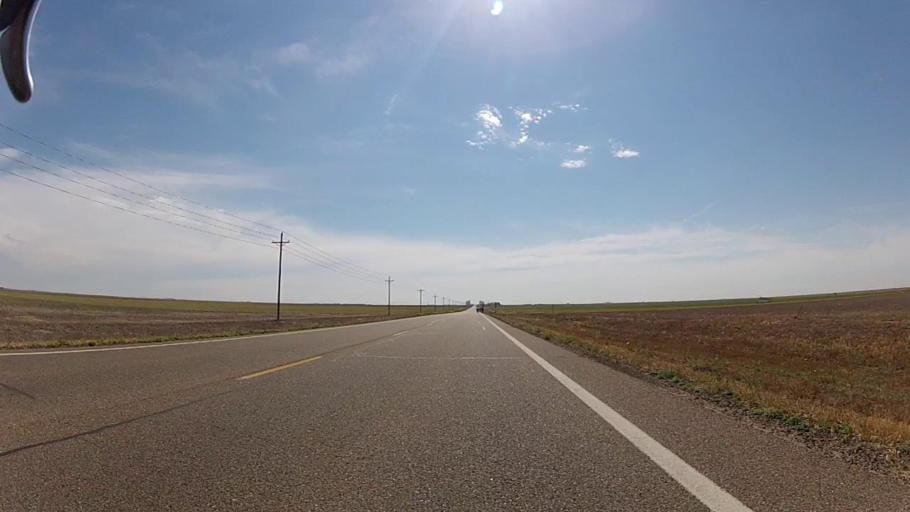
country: US
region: Kansas
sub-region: Grant County
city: Ulysses
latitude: 37.5617
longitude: -101.2829
